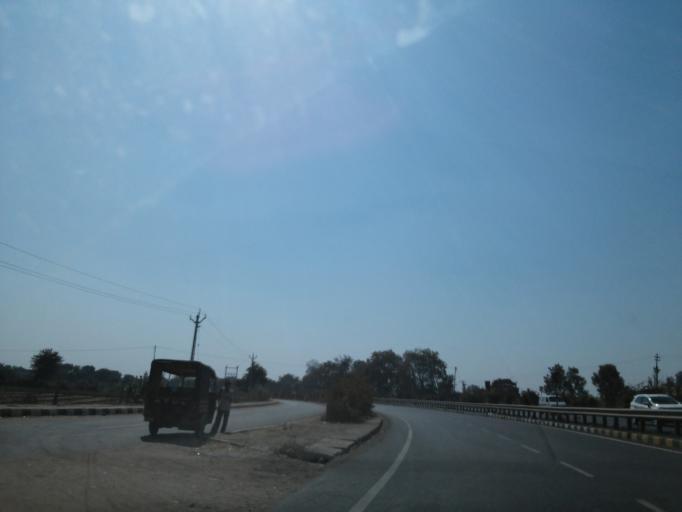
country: IN
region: Gujarat
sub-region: Gandhinagar
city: Chhala
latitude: 23.4423
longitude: 72.8442
